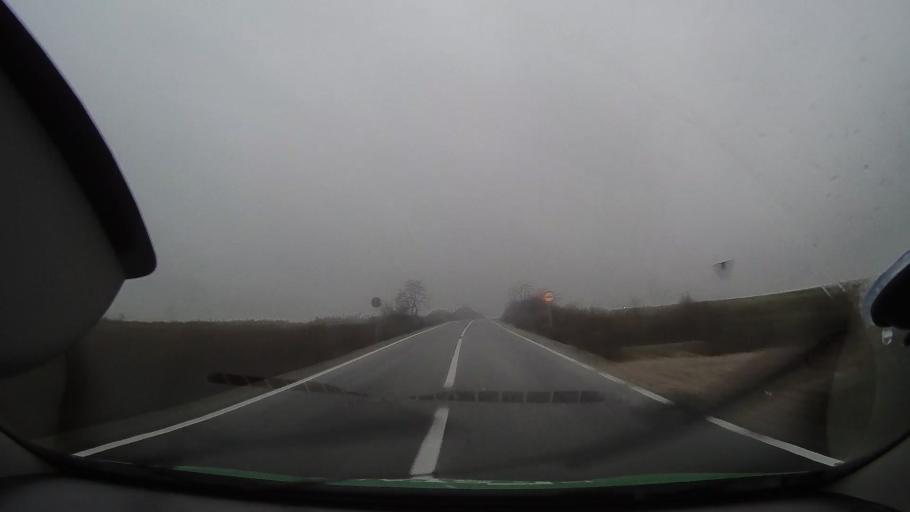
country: RO
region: Bihor
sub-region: Comuna Olcea
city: Calacea
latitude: 46.6462
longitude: 21.9574
